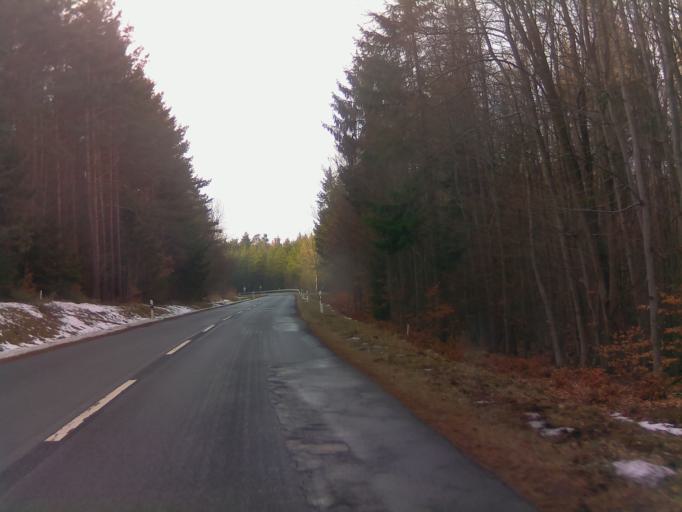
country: DE
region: Bavaria
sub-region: Regierungsbezirk Unterfranken
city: Sandberg
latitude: 50.3462
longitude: 10.0693
